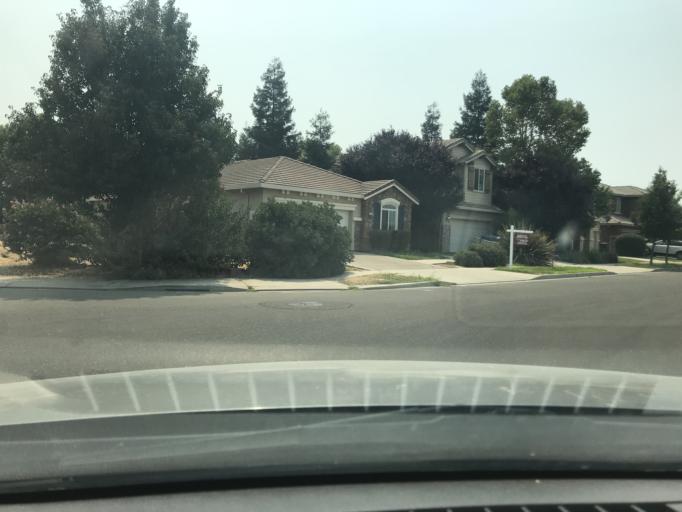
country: US
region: California
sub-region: Merced County
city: Merced
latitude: 37.3460
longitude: -120.4783
